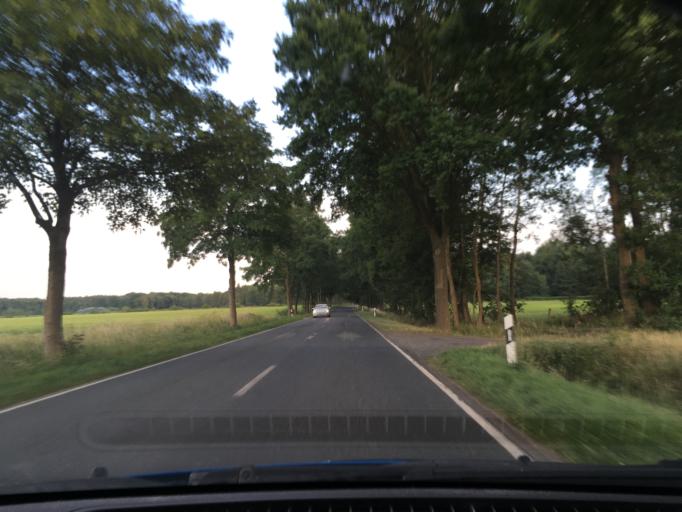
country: DE
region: Lower Saxony
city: Eldingen
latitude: 52.7011
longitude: 10.3259
